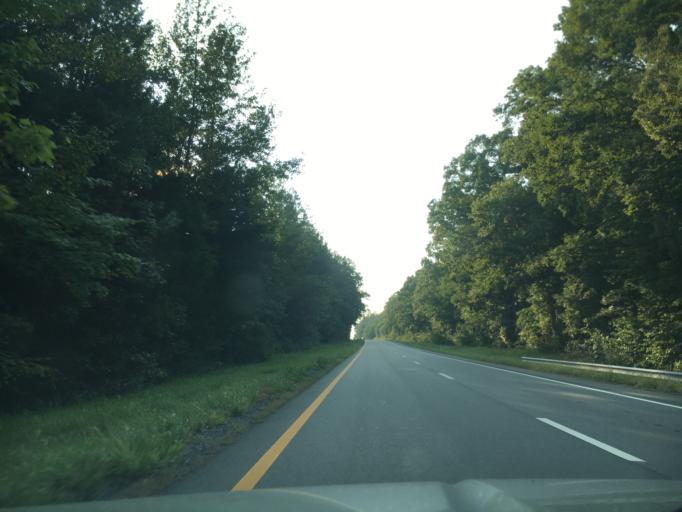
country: US
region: Virginia
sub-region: Appomattox County
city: Appomattox
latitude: 37.2746
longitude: -78.6818
